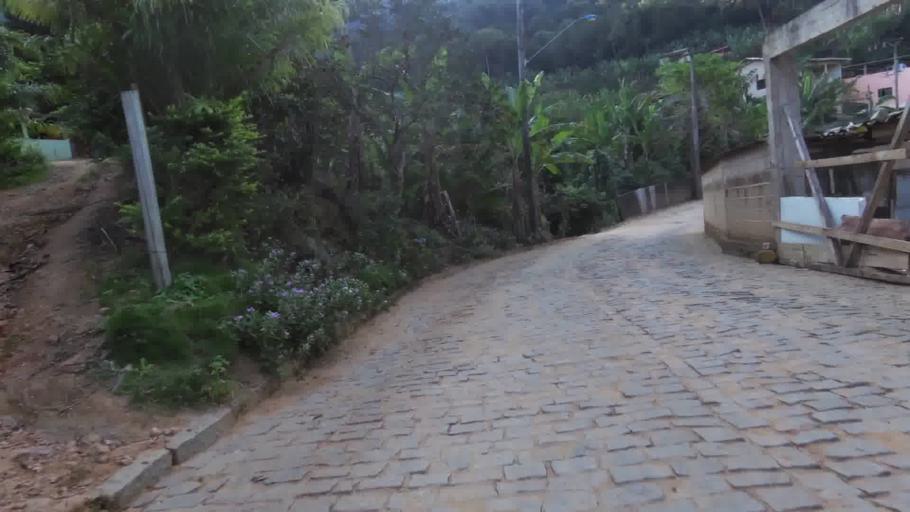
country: BR
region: Espirito Santo
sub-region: Alfredo Chaves
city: Alfredo Chaves
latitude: -20.5776
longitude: -40.6986
